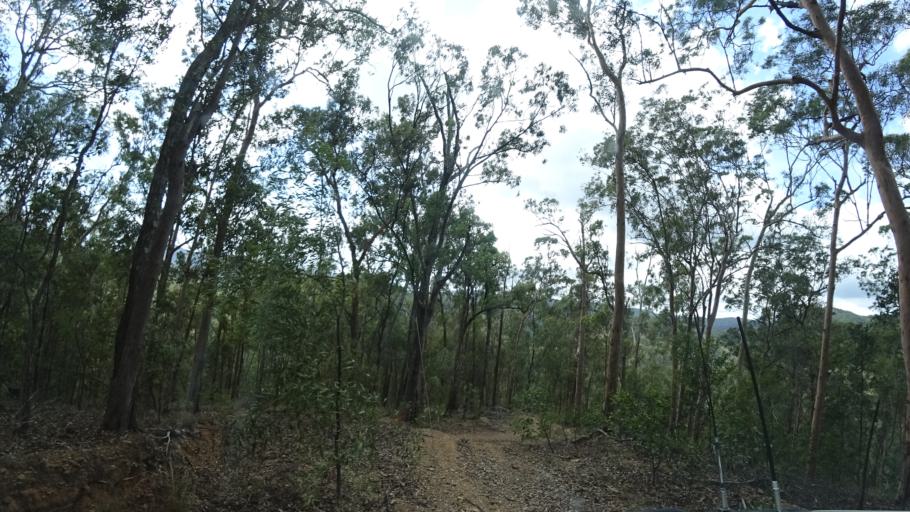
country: AU
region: Queensland
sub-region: Moreton Bay
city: Highvale
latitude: -27.3758
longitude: 152.7372
